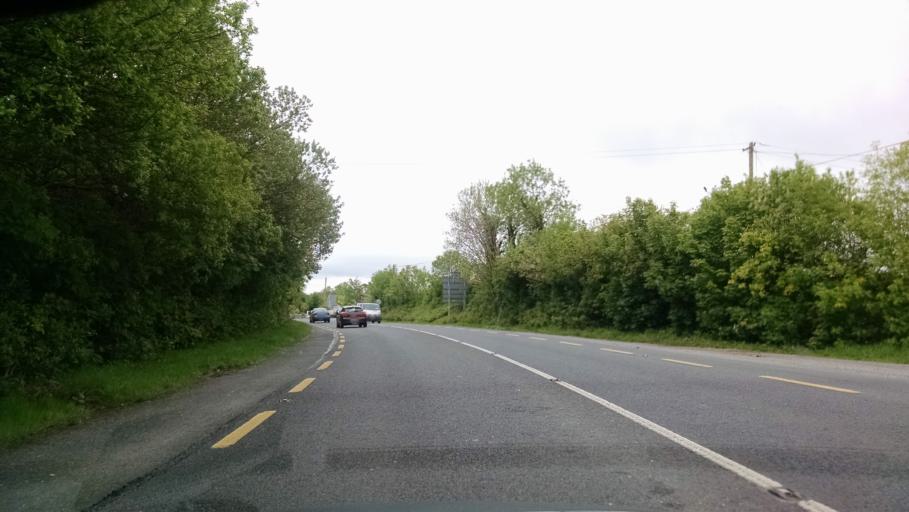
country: IE
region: Connaught
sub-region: County Galway
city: Moycullen
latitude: 53.4795
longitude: -9.0918
